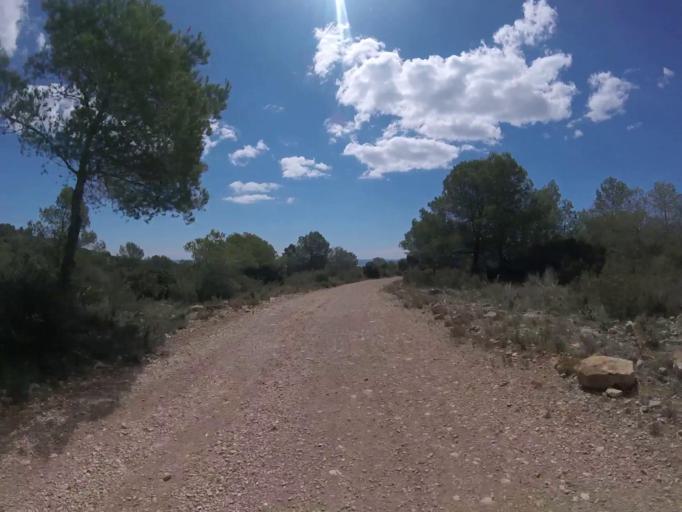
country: ES
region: Valencia
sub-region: Provincia de Castello
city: Alcoceber
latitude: 40.2877
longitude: 0.3192
